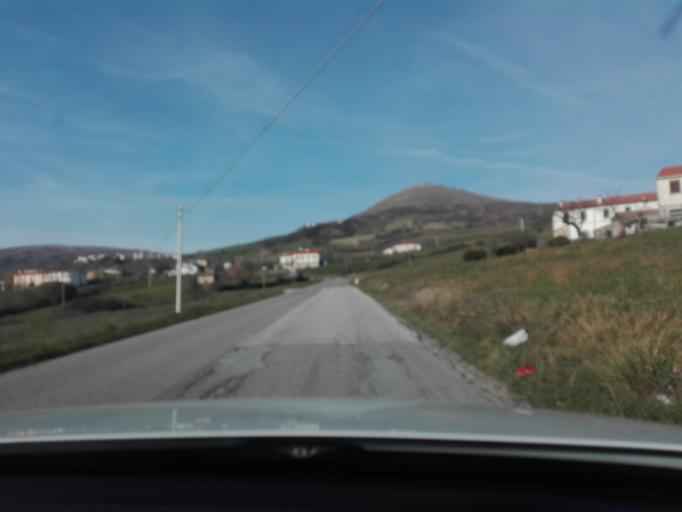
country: IT
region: Molise
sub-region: Provincia di Isernia
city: Agnone
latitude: 41.8346
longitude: 14.3831
